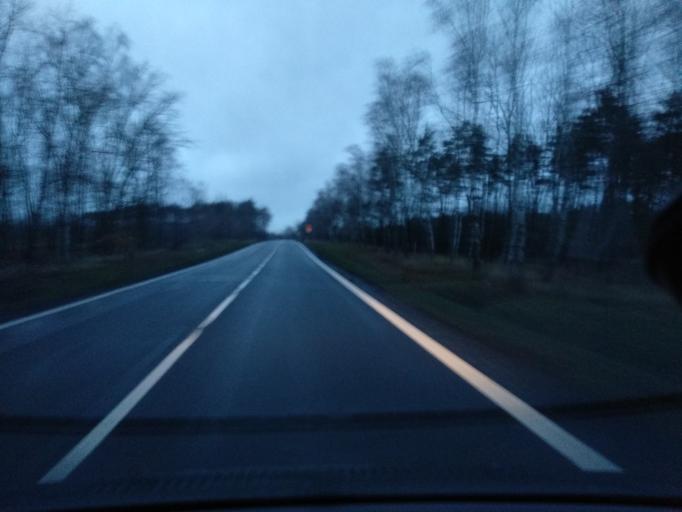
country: PL
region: Lower Silesian Voivodeship
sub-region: Powiat legnicki
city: Prochowice
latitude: 51.2573
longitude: 16.3963
